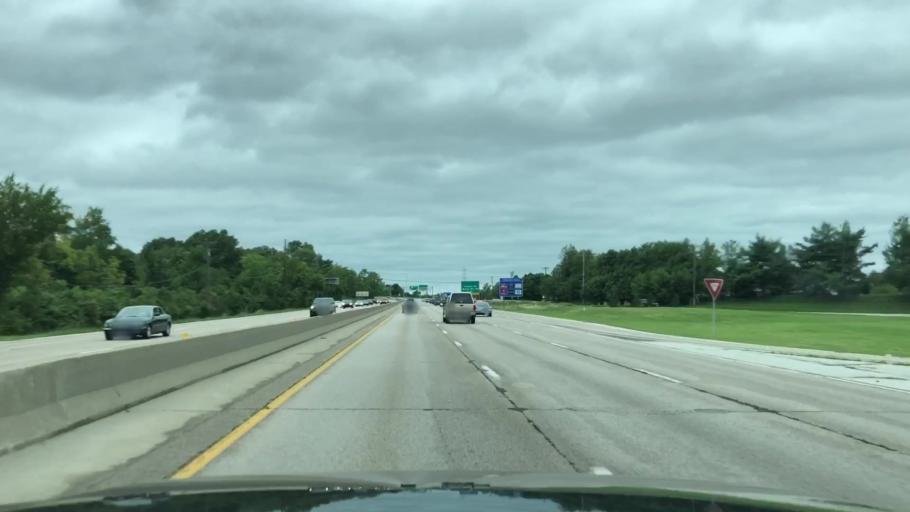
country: US
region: Missouri
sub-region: Saint Louis County
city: Manchester
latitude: 38.6344
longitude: -90.5132
